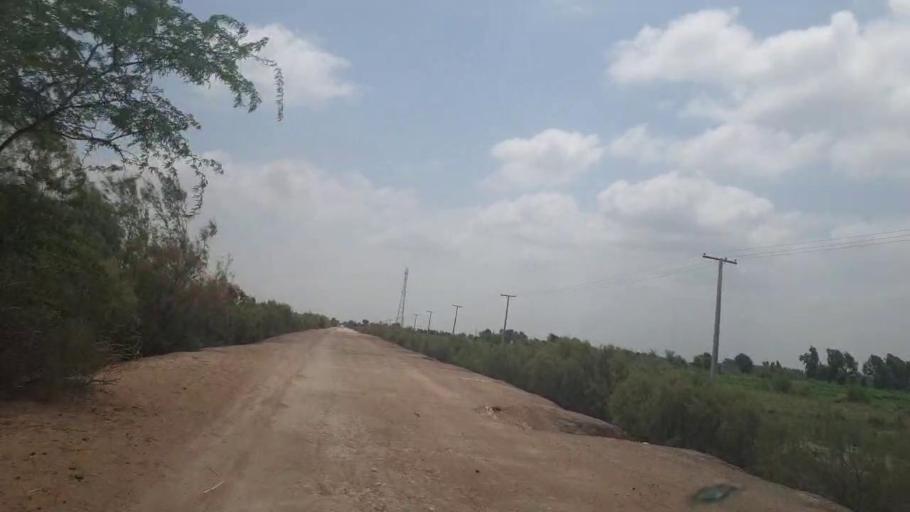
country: PK
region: Sindh
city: Tando Mittha Khan
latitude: 25.9174
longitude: 69.2193
